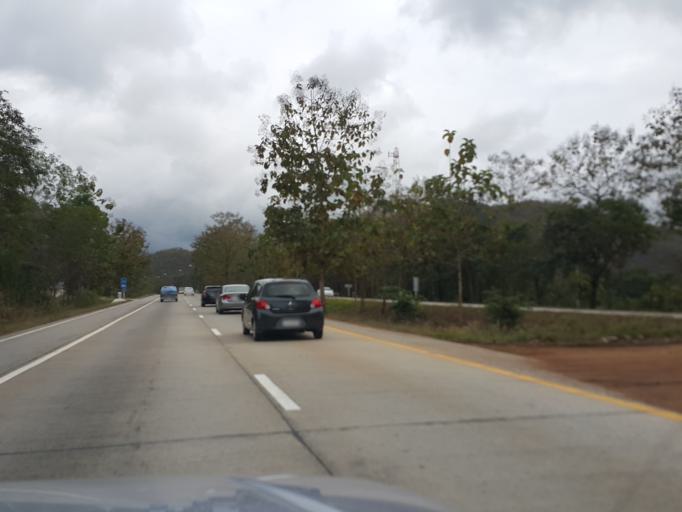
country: TH
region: Lamphun
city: Mae Tha
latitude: 18.5067
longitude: 99.1145
